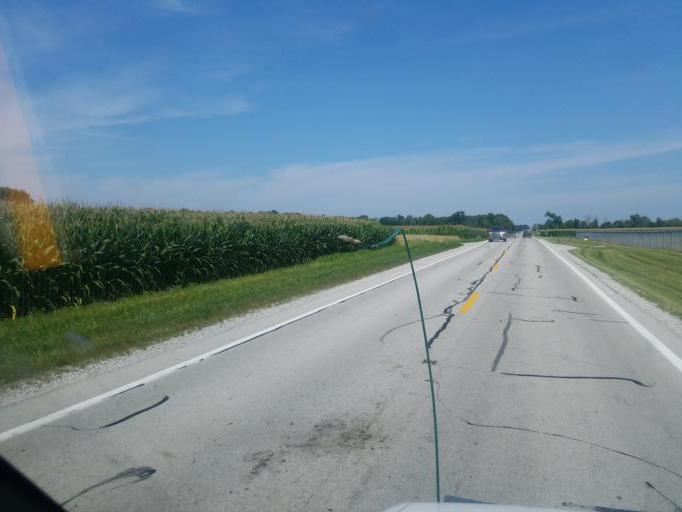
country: US
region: Ohio
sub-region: Auglaize County
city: New Bremen
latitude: 40.4962
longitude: -84.2874
